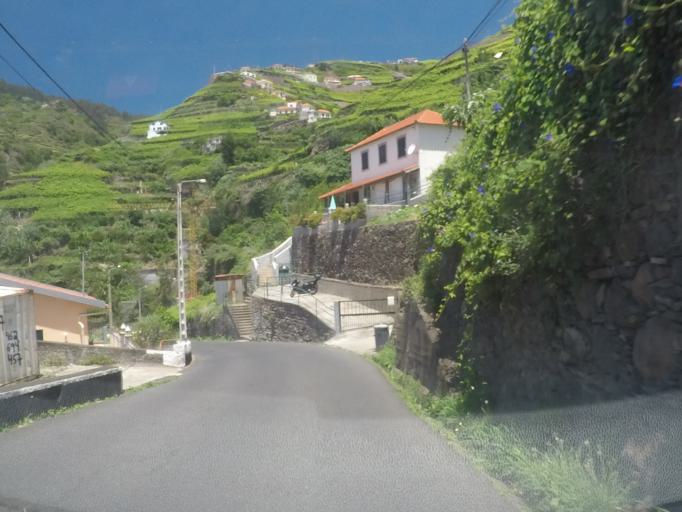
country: PT
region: Madeira
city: Camara de Lobos
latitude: 32.6716
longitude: -16.9847
